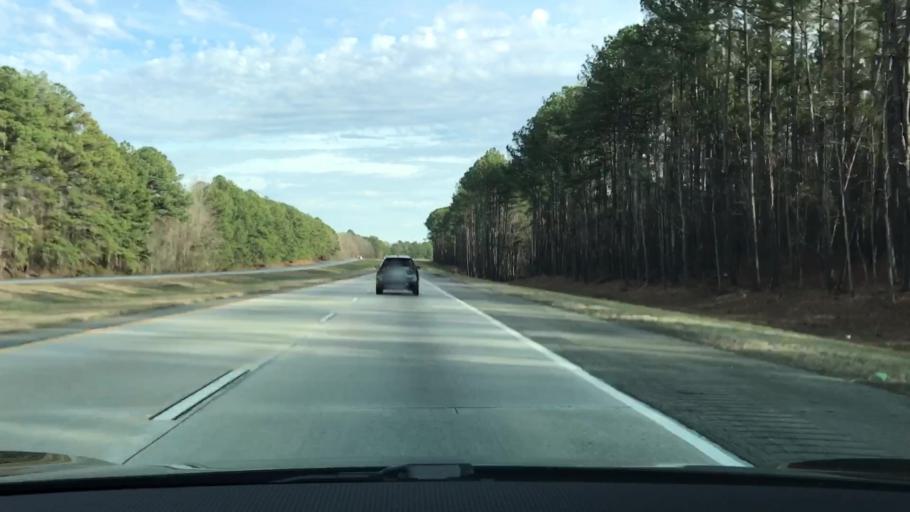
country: US
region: Georgia
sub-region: Greene County
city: Union Point
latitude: 33.5394
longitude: -83.0057
